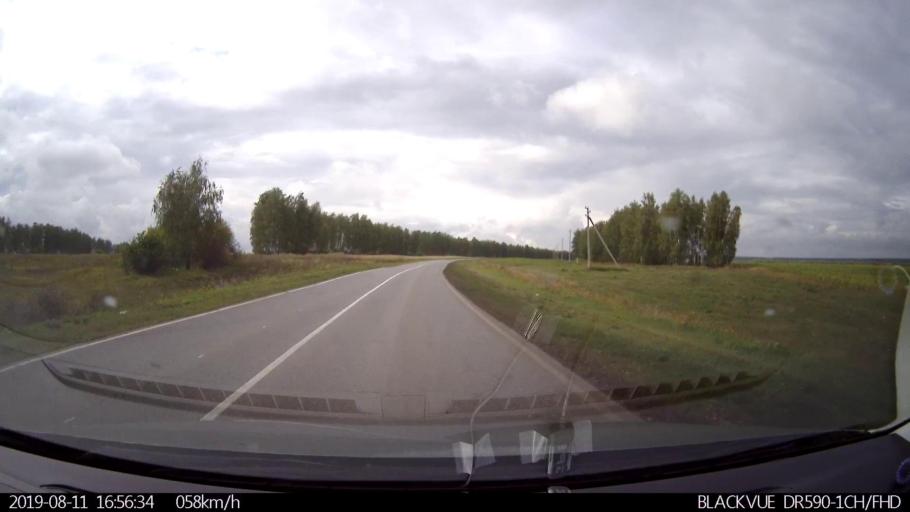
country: RU
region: Ulyanovsk
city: Mayna
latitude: 54.2885
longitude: 47.6527
